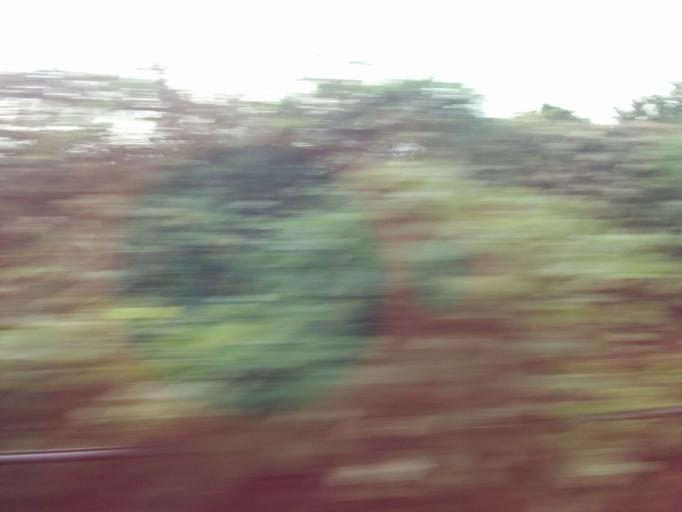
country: JP
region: Shizuoka
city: Fuji
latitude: 35.1538
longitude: 138.7686
